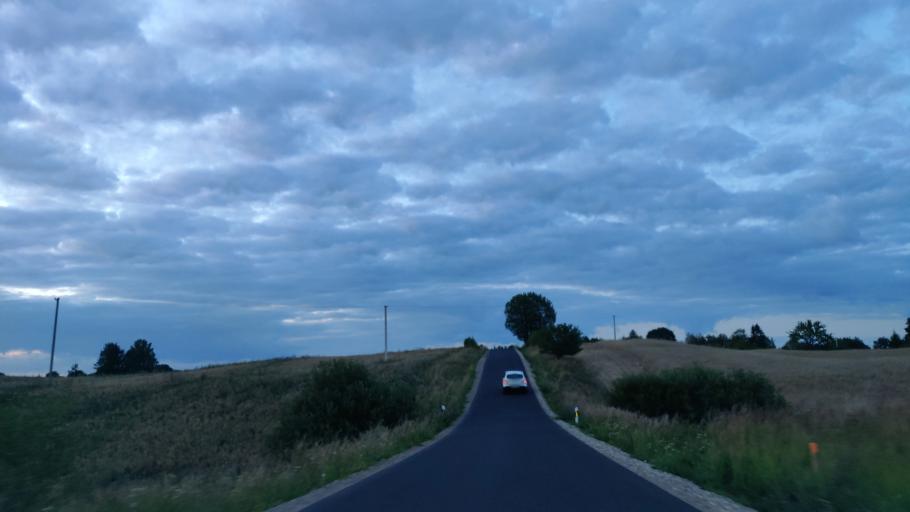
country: LT
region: Vilnius County
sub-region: Trakai
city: Rudiskes
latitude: 54.6176
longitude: 24.8122
